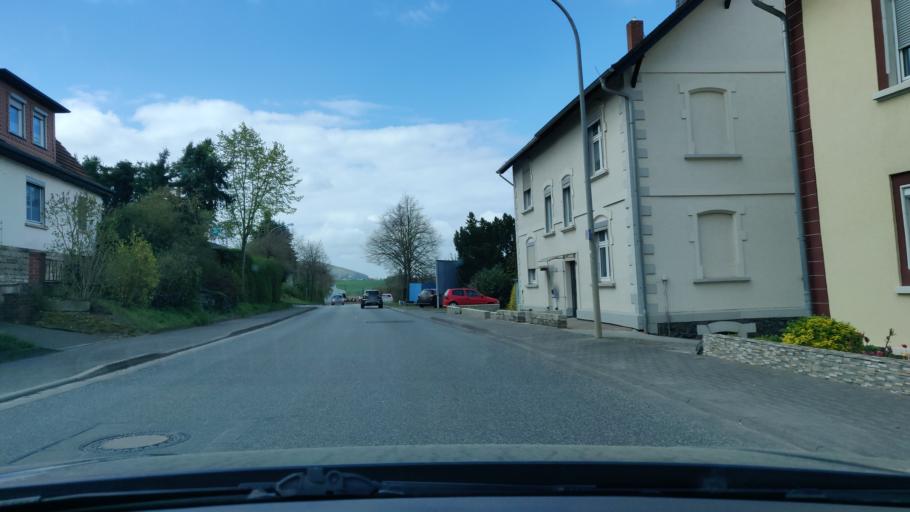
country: DE
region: Hesse
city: Felsberg
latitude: 51.1261
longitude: 9.4326
